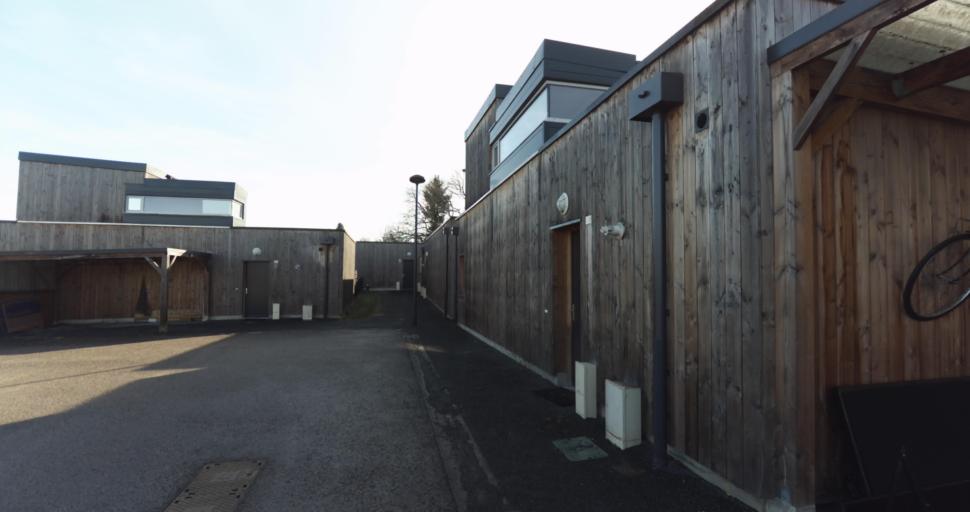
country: FR
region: Limousin
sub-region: Departement de la Haute-Vienne
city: Aixe-sur-Vienne
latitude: 45.7927
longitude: 1.1243
